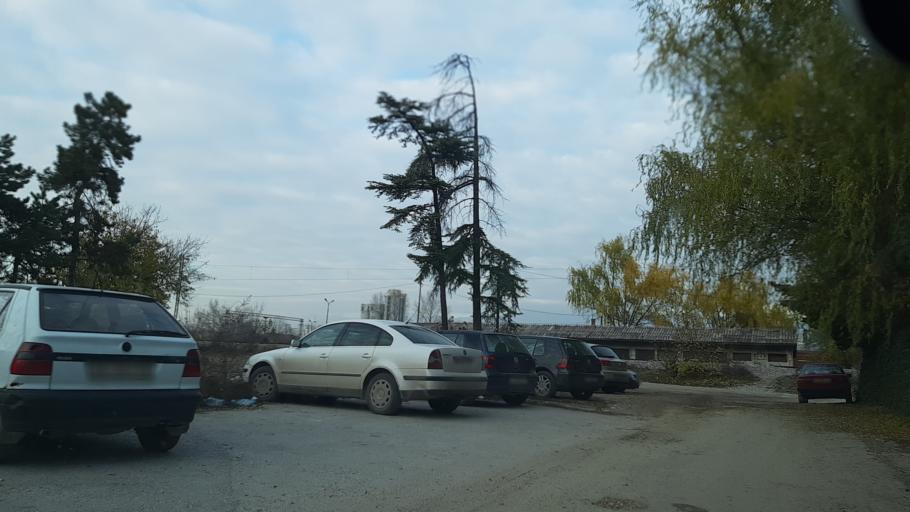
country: MK
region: Karpos
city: Skopje
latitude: 41.9801
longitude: 21.4482
